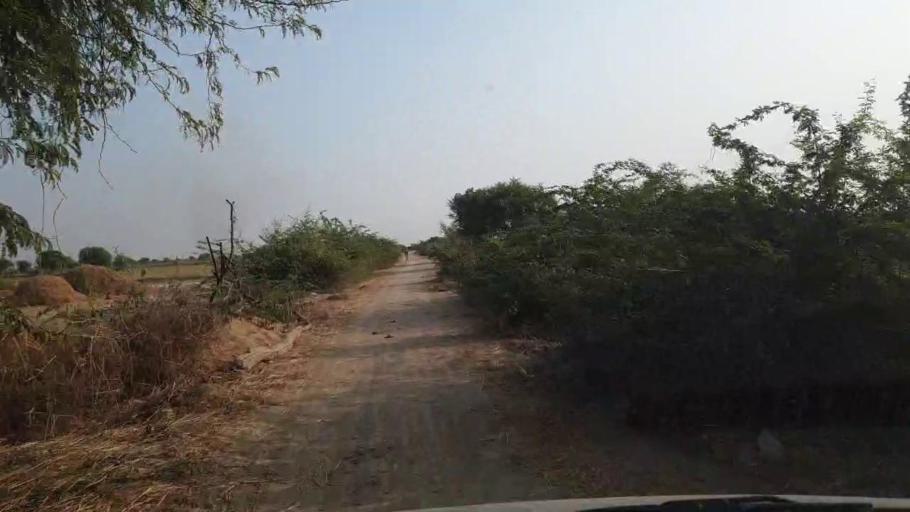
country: PK
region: Sindh
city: Rajo Khanani
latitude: 25.0314
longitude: 68.7774
